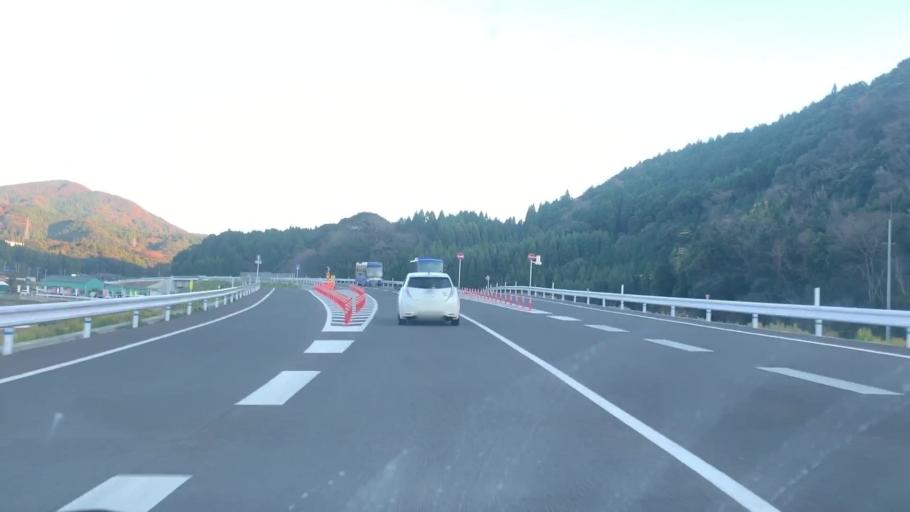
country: JP
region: Saga Prefecture
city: Takeocho-takeo
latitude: 33.2508
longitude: 129.9922
